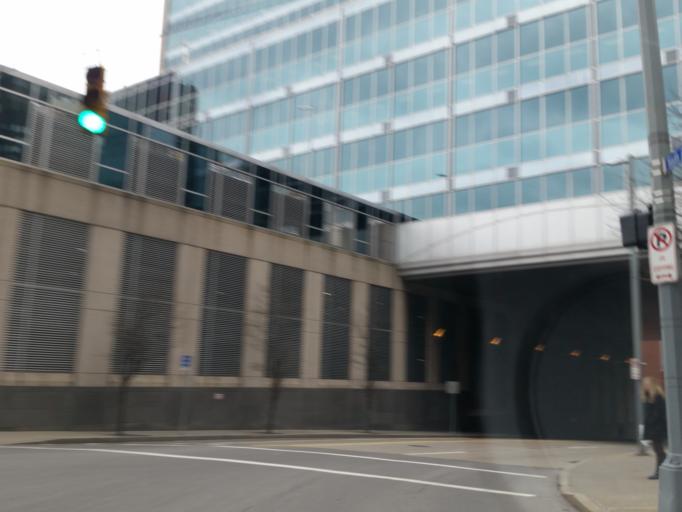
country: US
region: Pennsylvania
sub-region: Allegheny County
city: Pittsburgh
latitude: 40.4400
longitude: -79.9943
